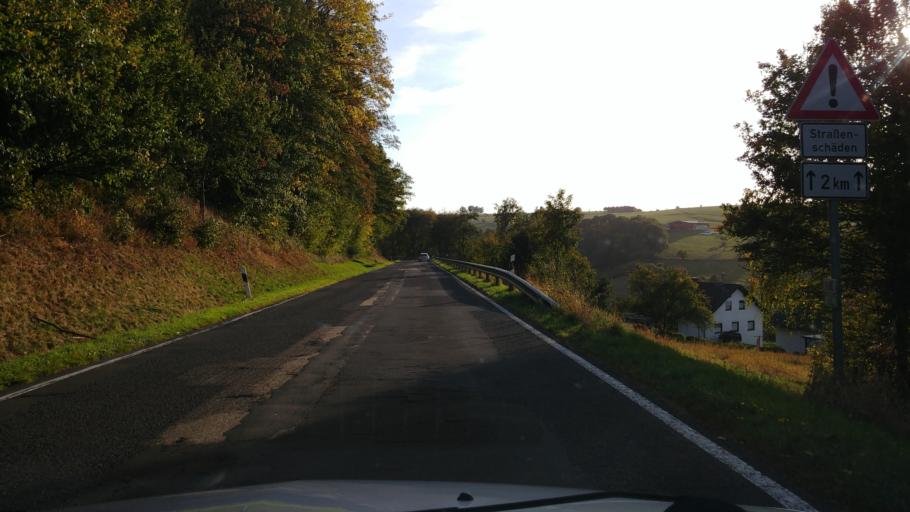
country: DE
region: Rheinland-Pfalz
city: Gornhausen
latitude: 49.8224
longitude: 7.0673
